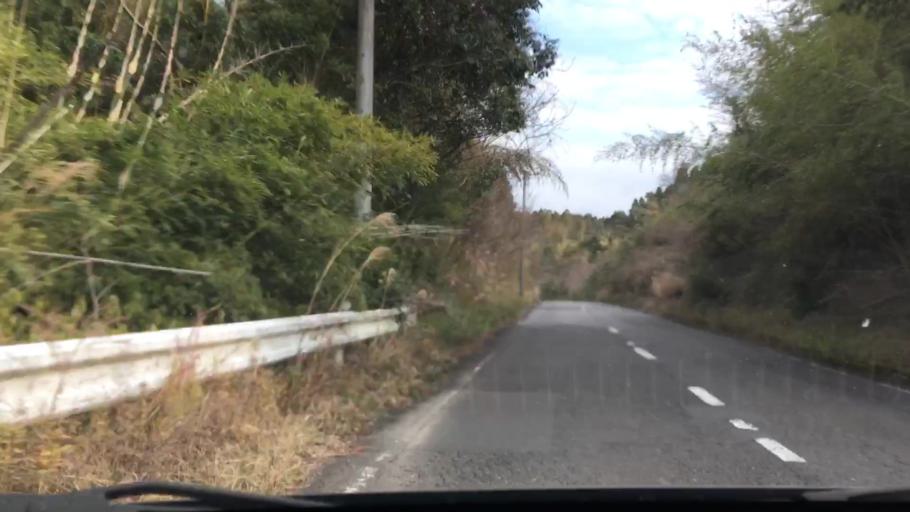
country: JP
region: Miyazaki
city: Nichinan
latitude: 31.6099
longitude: 131.3321
